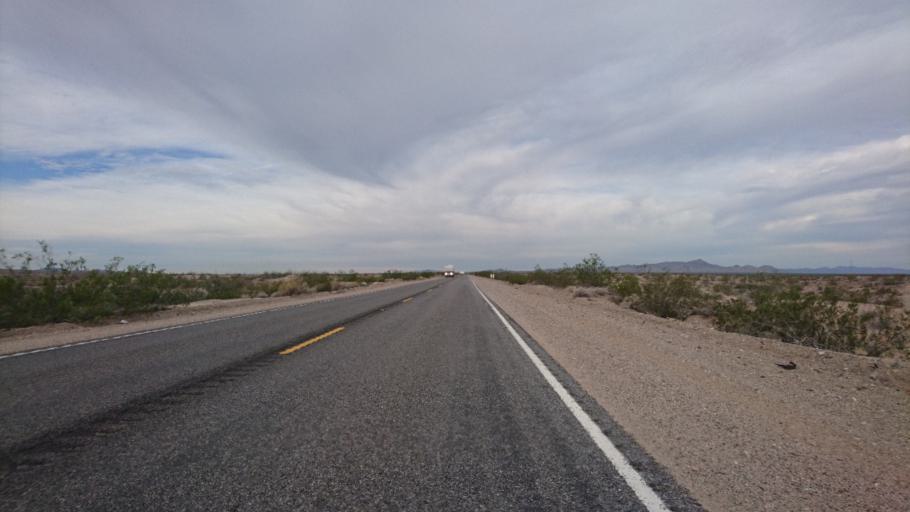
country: US
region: Arizona
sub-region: Mohave County
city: Willow Valley
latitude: 34.9323
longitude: -114.7956
